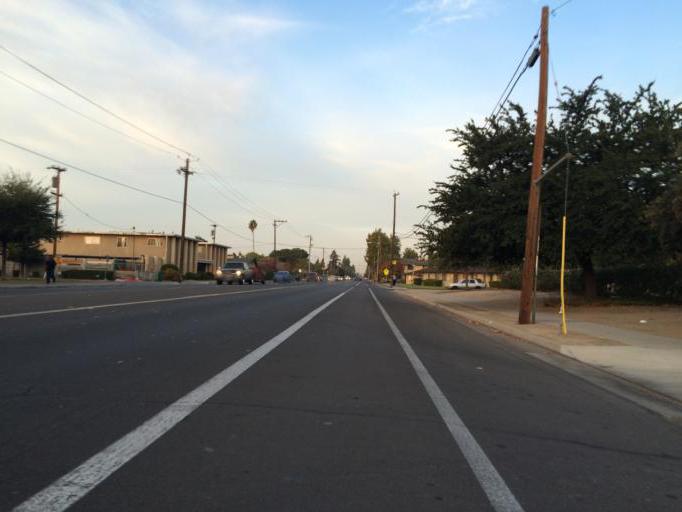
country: US
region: California
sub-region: Fresno County
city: Fresno
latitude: 36.7869
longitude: -119.7560
